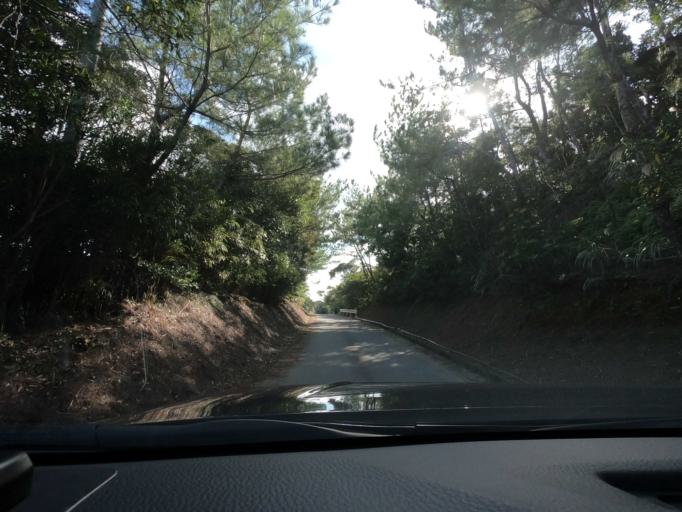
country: JP
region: Okinawa
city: Nago
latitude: 26.7553
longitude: 128.2058
